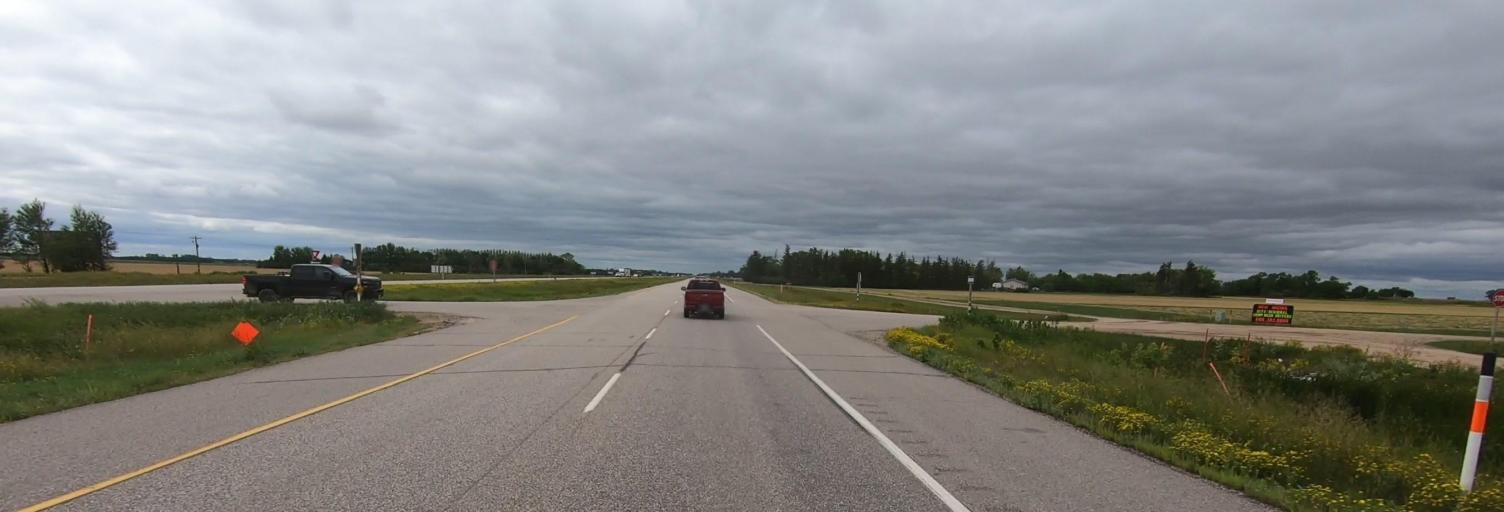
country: CA
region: Manitoba
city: Portage la Prairie
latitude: 49.9752
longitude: -98.4222
